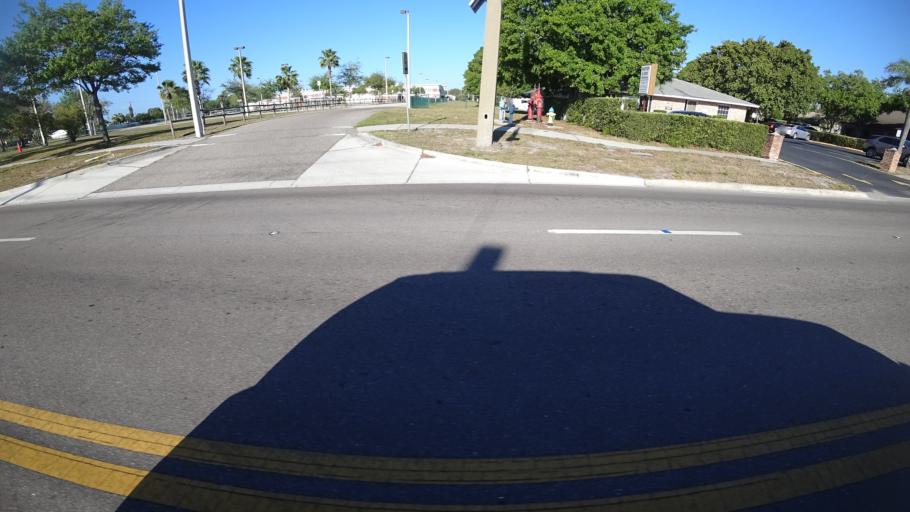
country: US
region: Florida
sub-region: Manatee County
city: Bayshore Gardens
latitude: 27.4327
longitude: -82.5878
